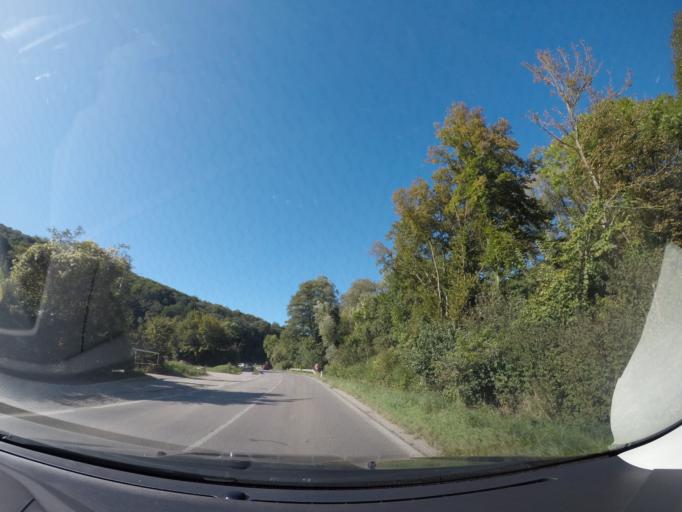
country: AT
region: Lower Austria
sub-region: Politischer Bezirk Modling
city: Laab im Walde
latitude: 48.1451
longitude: 16.1936
